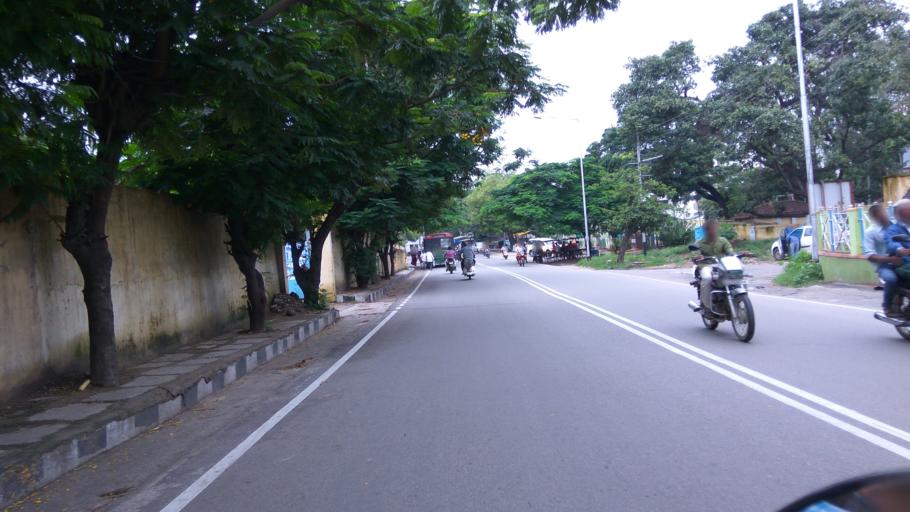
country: IN
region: Telangana
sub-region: Hyderabad
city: Malkajgiri
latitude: 17.4363
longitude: 78.5206
